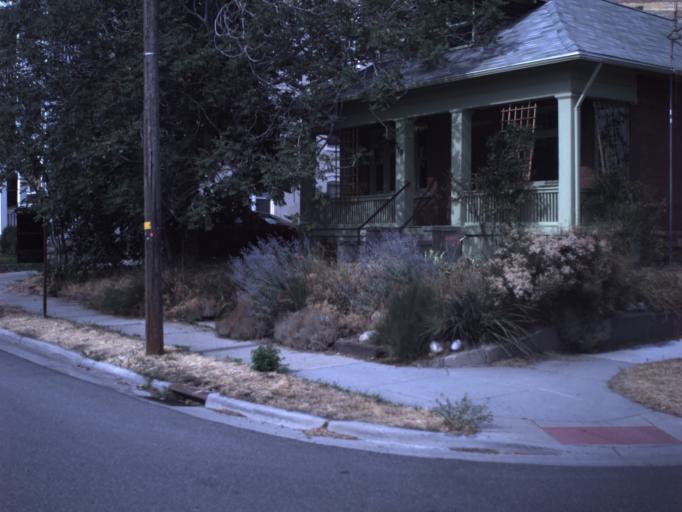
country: US
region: Utah
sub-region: Salt Lake County
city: Salt Lake City
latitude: 40.7857
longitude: -111.8996
